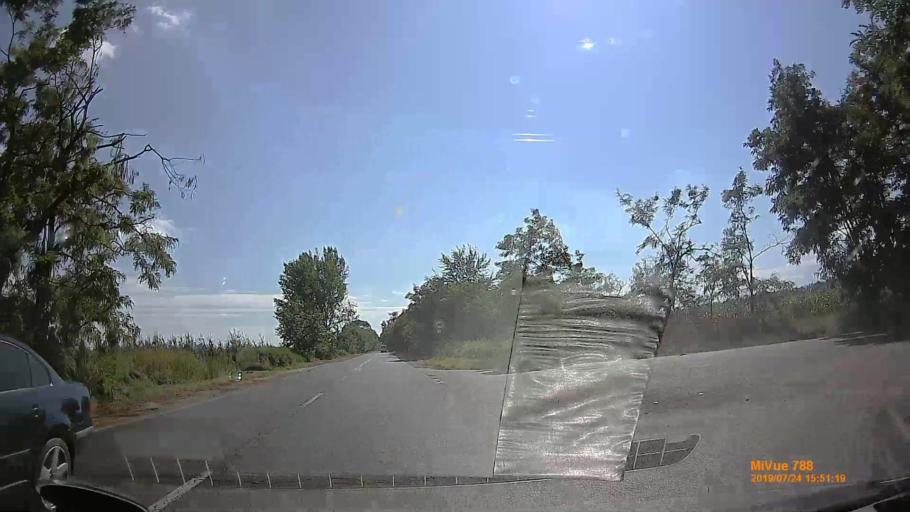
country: HU
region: Szabolcs-Szatmar-Bereg
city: Nyirmada
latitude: 48.0416
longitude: 22.1850
